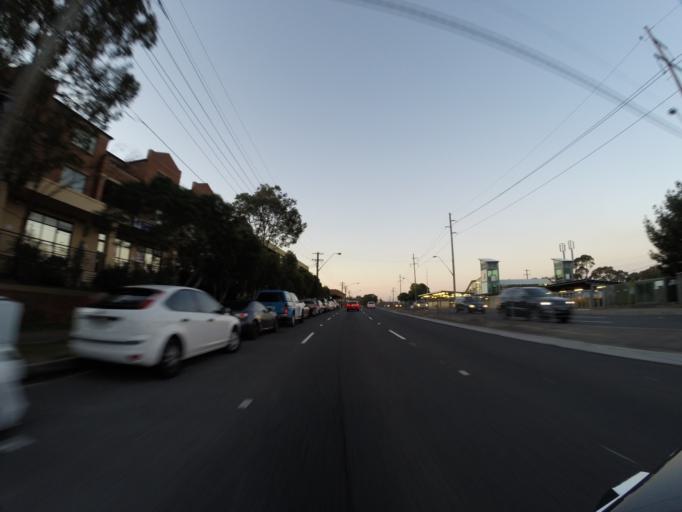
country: AU
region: New South Wales
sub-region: Sutherland Shire
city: Engadine
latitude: -34.0681
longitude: 151.0141
